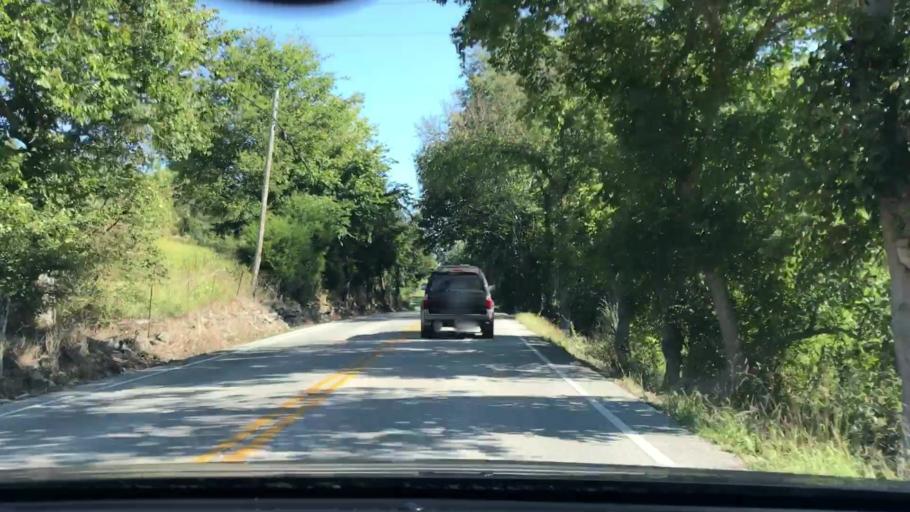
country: US
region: Tennessee
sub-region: Smith County
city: Carthage
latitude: 36.3471
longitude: -85.8972
